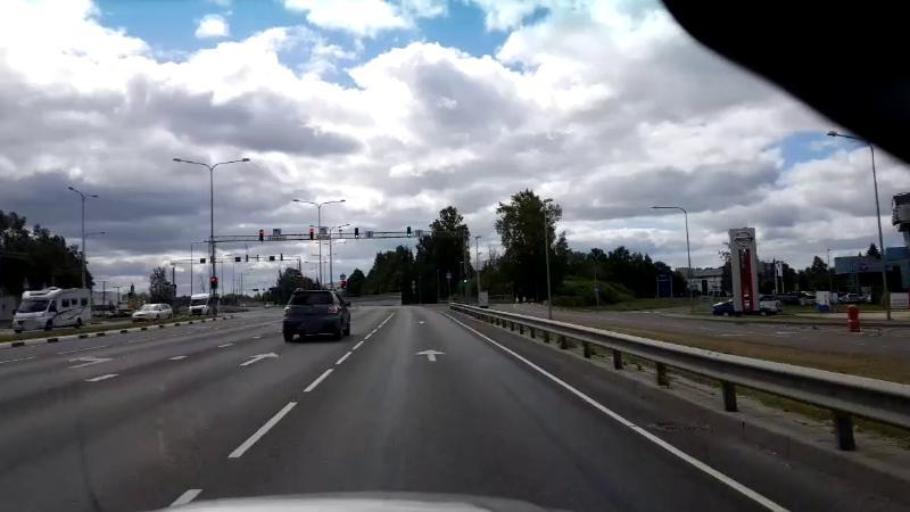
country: EE
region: Paernumaa
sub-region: Paernu linn
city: Parnu
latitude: 58.4047
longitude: 24.5010
